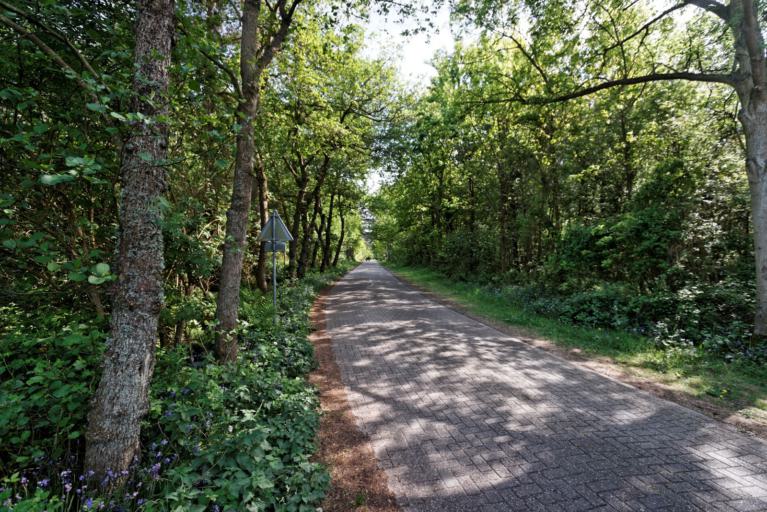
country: NL
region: North Holland
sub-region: Gemeente Texel
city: Den Burg
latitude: 53.0686
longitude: 4.7508
